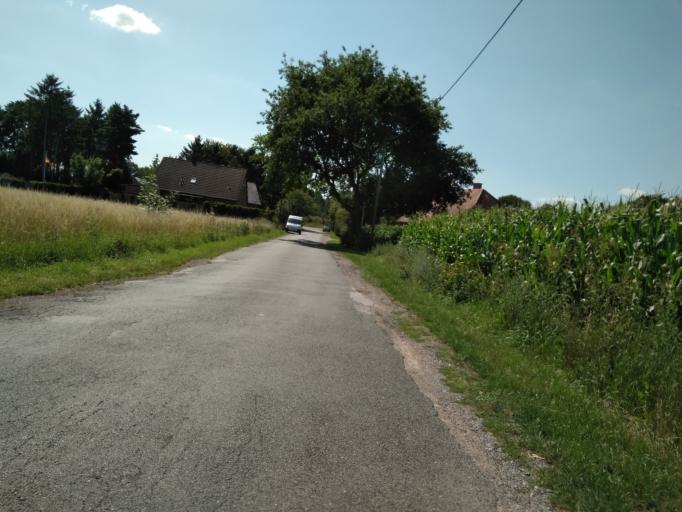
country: DE
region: North Rhine-Westphalia
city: Dorsten
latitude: 51.6874
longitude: 6.9532
